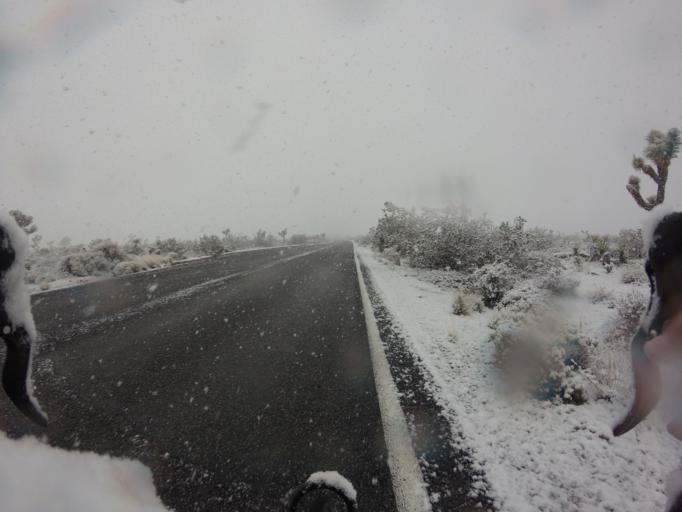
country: US
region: California
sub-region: San Bernardino County
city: Twentynine Palms
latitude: 34.0129
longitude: -116.0342
